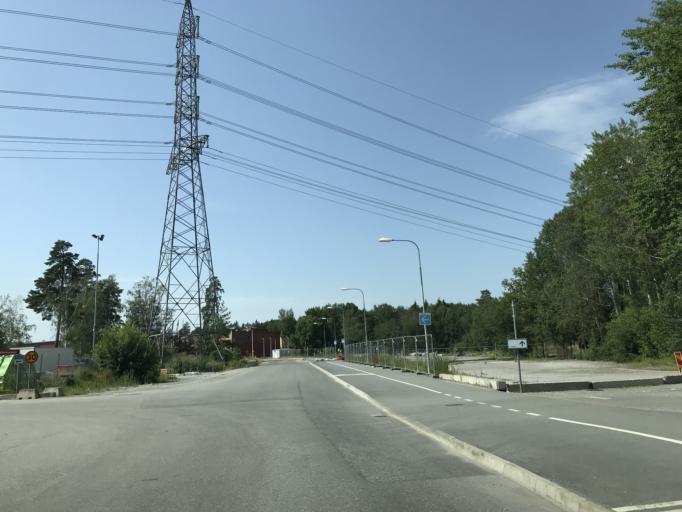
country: SE
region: Stockholm
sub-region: Solna Kommun
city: Rasunda
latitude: 59.3829
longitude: 17.9913
